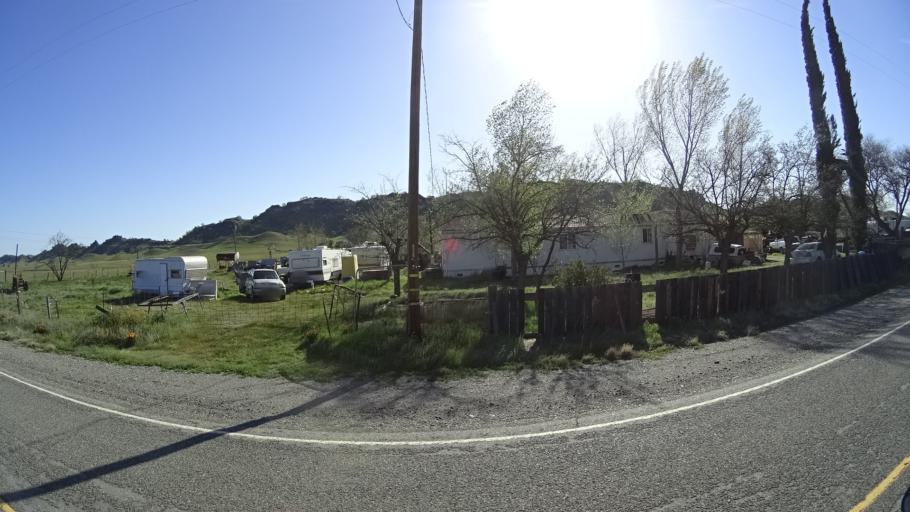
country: US
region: California
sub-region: Tehama County
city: Rancho Tehama Reserve
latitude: 39.7268
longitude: -122.5497
